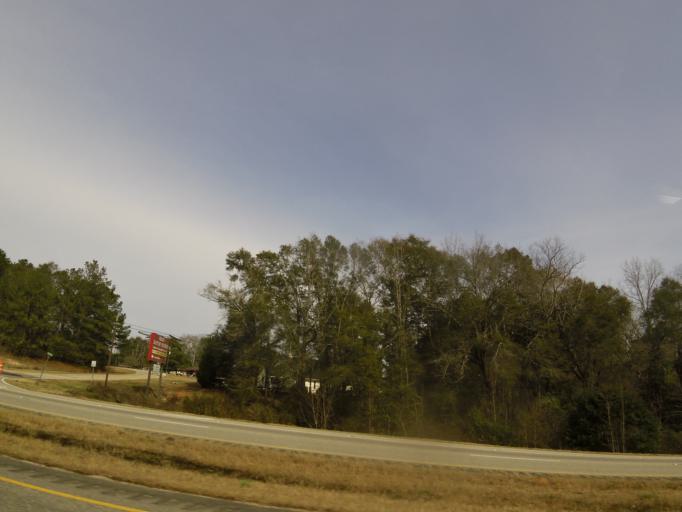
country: US
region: Alabama
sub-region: Dale County
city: Ozark
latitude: 31.4209
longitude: -85.6121
